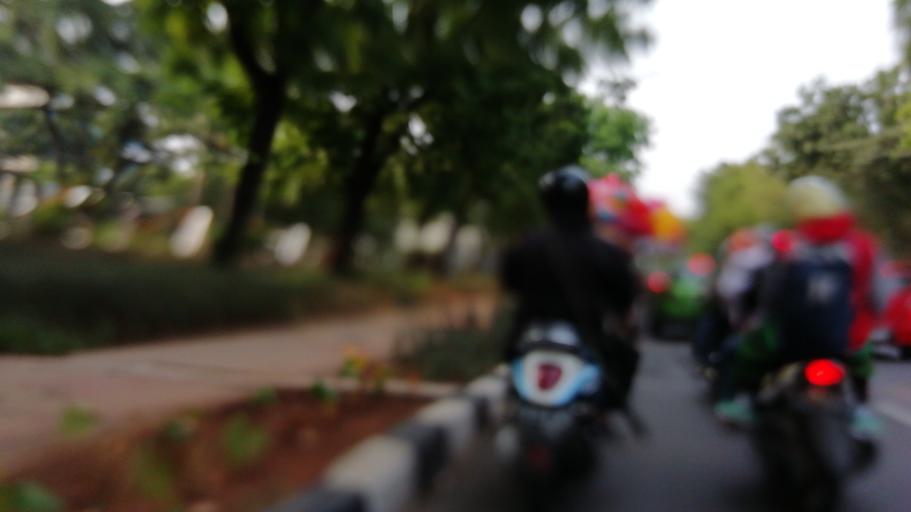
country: ID
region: West Java
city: Depok
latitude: -6.3403
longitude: 106.8338
